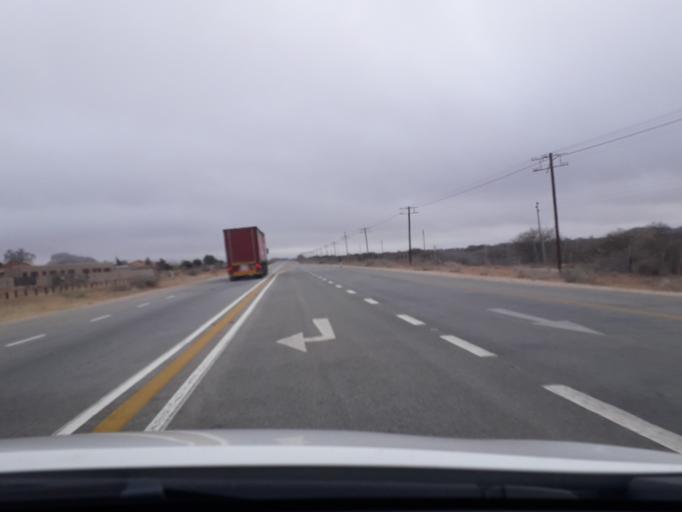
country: ZA
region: Limpopo
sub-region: Capricorn District Municipality
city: Mankoeng
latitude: -23.5197
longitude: 29.7098
